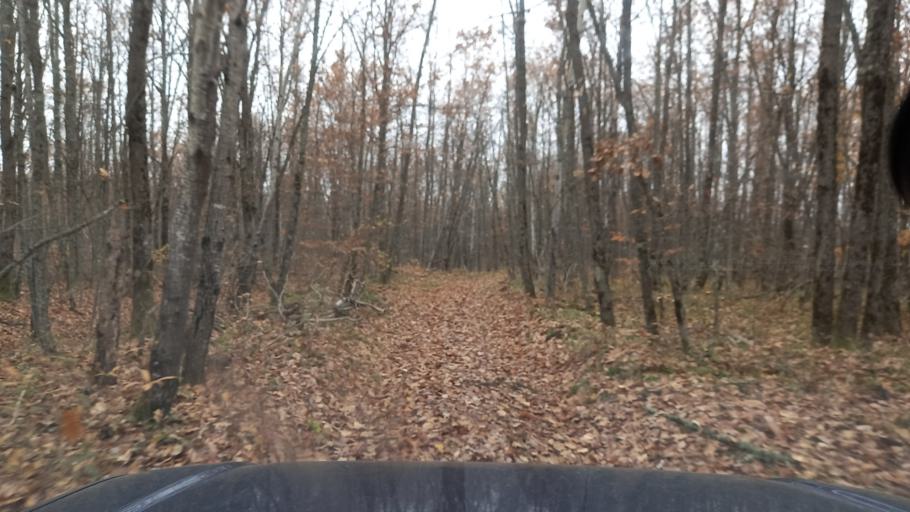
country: RU
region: Krasnodarskiy
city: Goryachiy Klyuch
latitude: 44.4984
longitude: 39.2765
